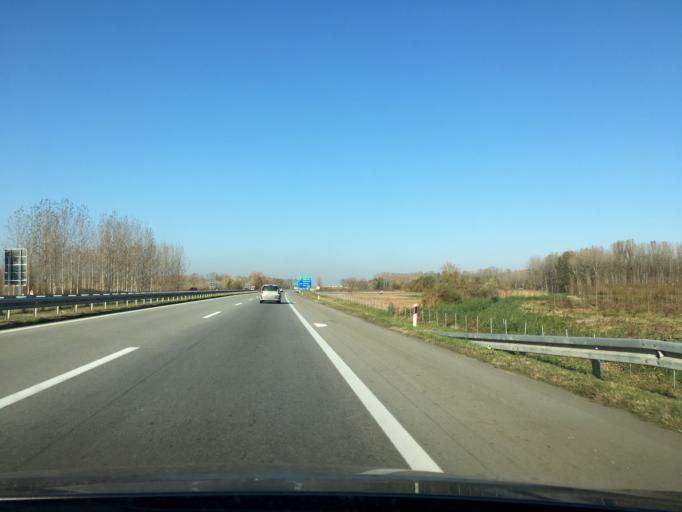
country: RS
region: Autonomna Pokrajina Vojvodina
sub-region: Juznobacki Okrug
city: Petrovaradin
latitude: 45.2818
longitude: 19.9040
